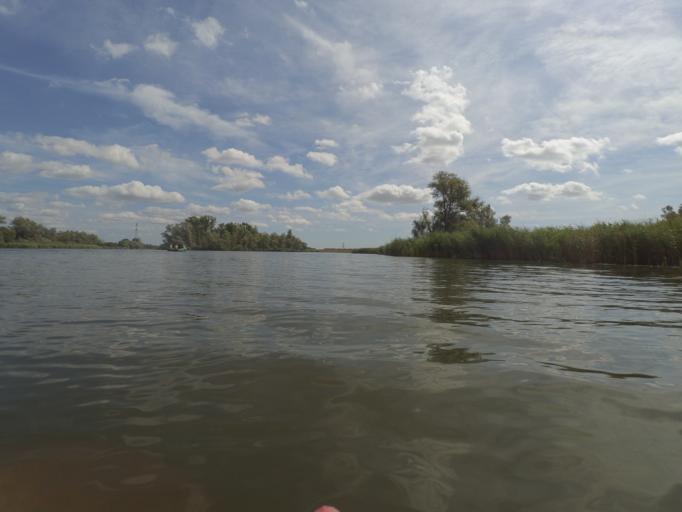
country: NL
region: North Brabant
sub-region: Gemeente Geertruidenberg
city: Geertruidenberg
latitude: 51.7564
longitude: 4.8461
